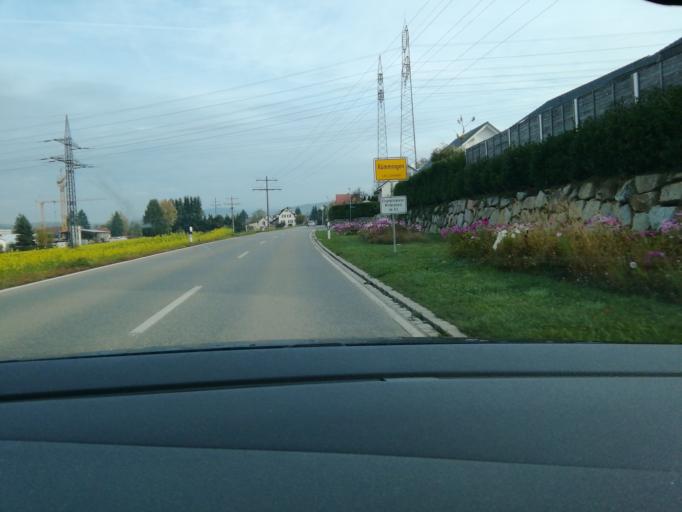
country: DE
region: Baden-Wuerttemberg
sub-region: Freiburg Region
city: Schallbach
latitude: 47.6390
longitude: 7.6389
